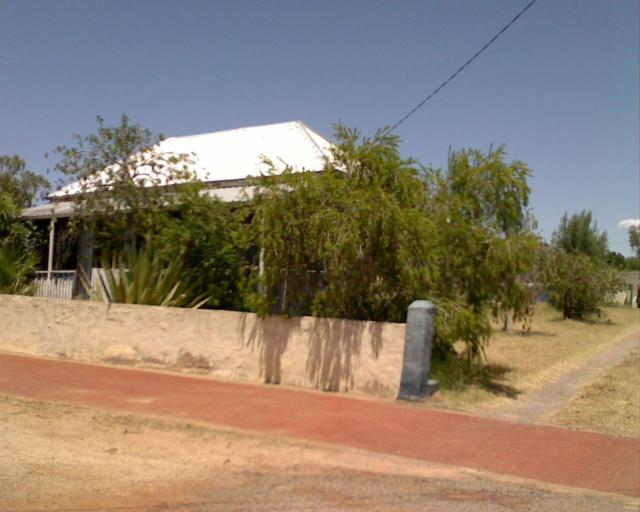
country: AU
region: Western Australia
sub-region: Irwin
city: Dongara
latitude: -29.1907
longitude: 115.4421
